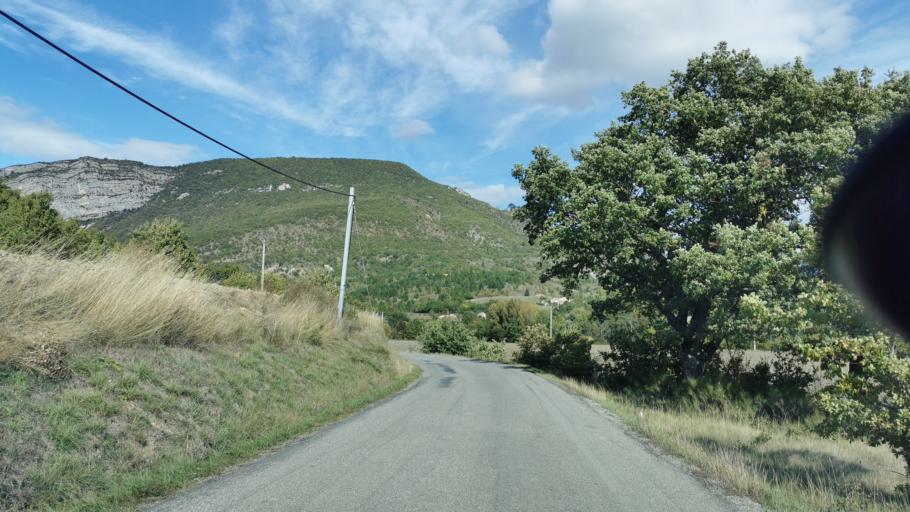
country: FR
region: Provence-Alpes-Cote d'Azur
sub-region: Departement des Alpes-de-Haute-Provence
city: Sisteron
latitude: 44.1834
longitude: 5.9933
